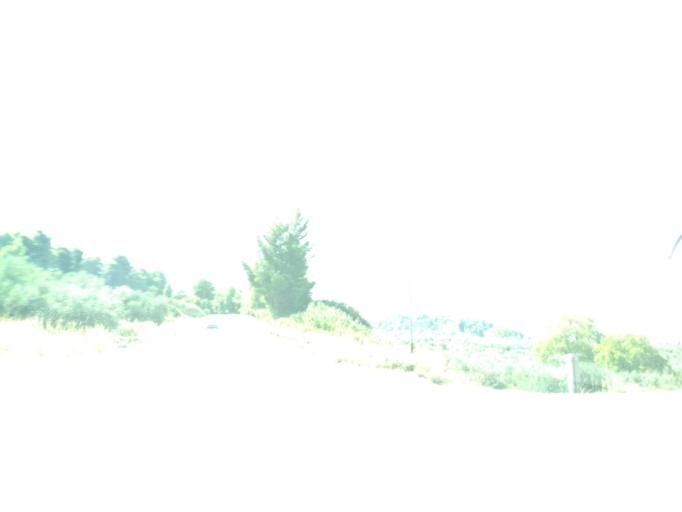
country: GR
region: Central Greece
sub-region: Nomos Evvoias
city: Roviai
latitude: 38.8274
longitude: 23.2248
